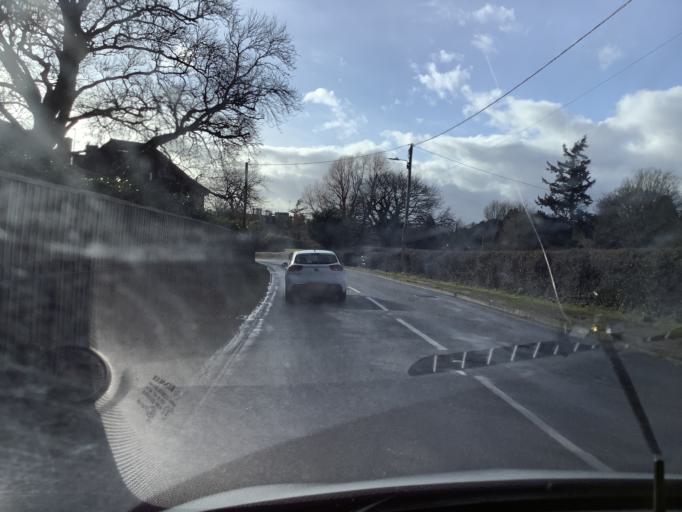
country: GB
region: England
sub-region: Hampshire
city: Hythe
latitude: 50.8203
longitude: -1.4472
